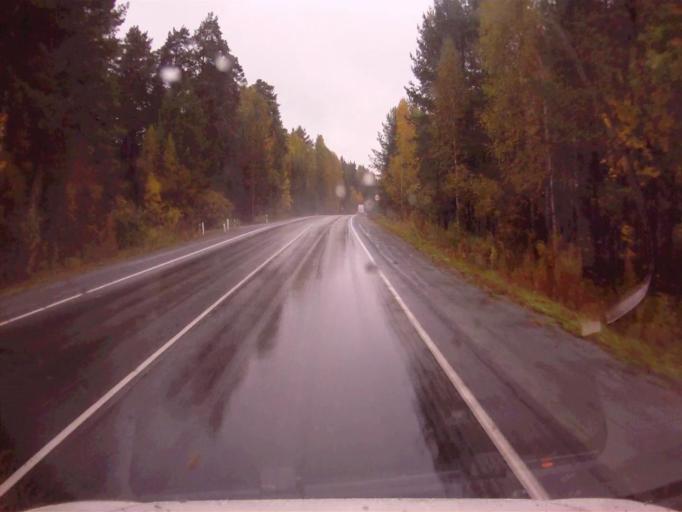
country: RU
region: Chelyabinsk
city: Tayginka
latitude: 55.5566
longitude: 60.6462
